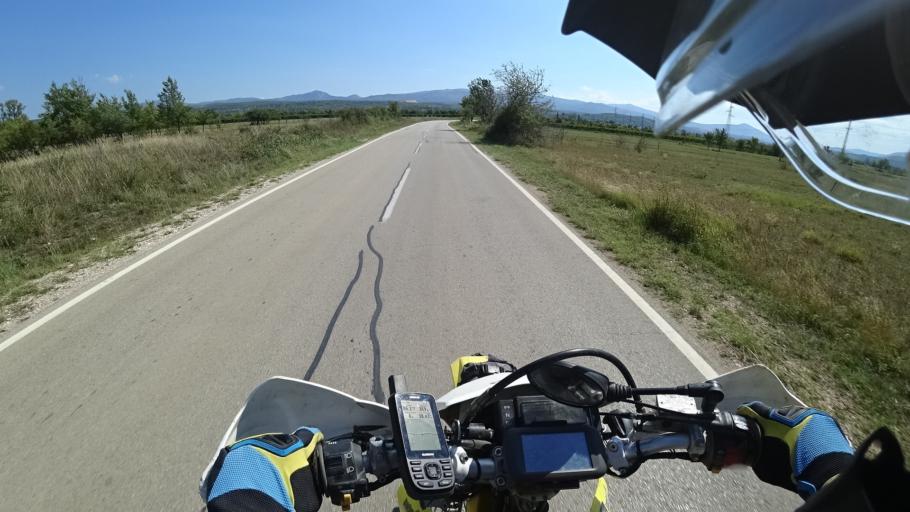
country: HR
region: Sibensko-Kniniska
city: Drnis
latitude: 43.8656
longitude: 16.1996
